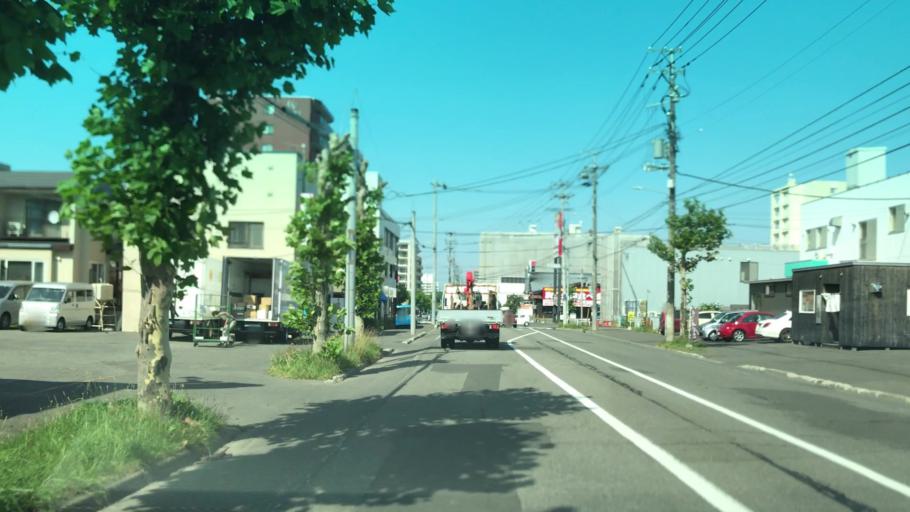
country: JP
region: Hokkaido
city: Sapporo
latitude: 43.0925
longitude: 141.2709
